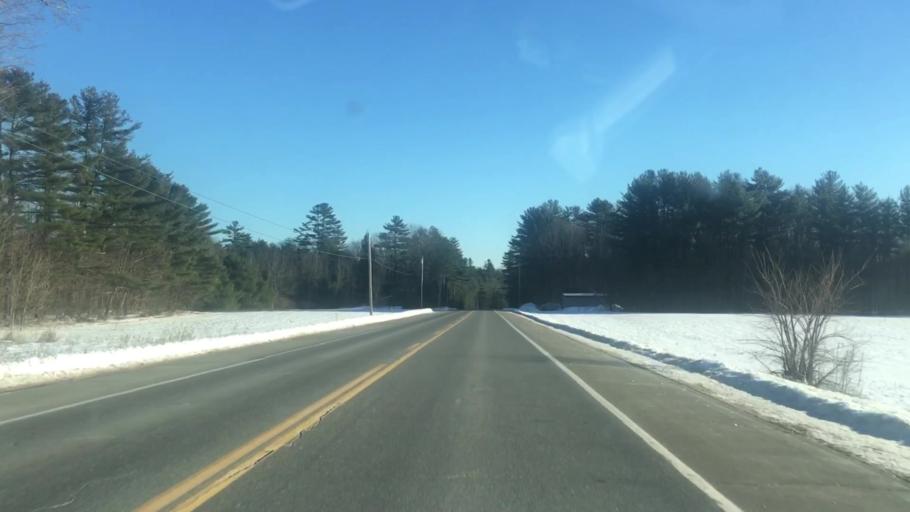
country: US
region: Maine
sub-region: Somerset County
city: Norridgewock
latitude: 44.7475
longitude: -69.8344
